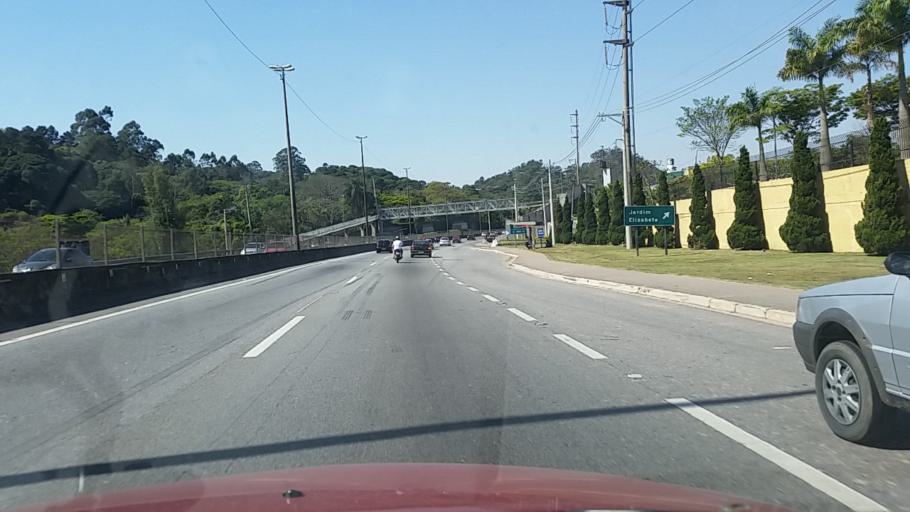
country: BR
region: Sao Paulo
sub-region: Taboao Da Serra
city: Taboao da Serra
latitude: -23.6194
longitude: -46.8098
